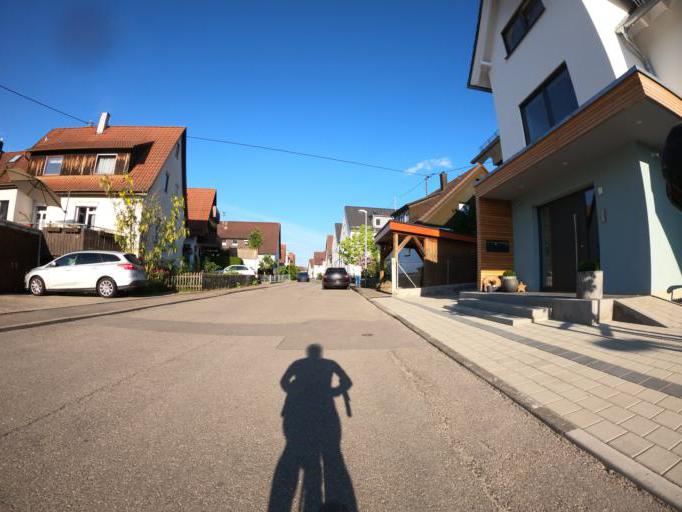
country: DE
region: Baden-Wuerttemberg
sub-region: Regierungsbezirk Stuttgart
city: Ehningen
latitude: 48.6969
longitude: 8.9357
